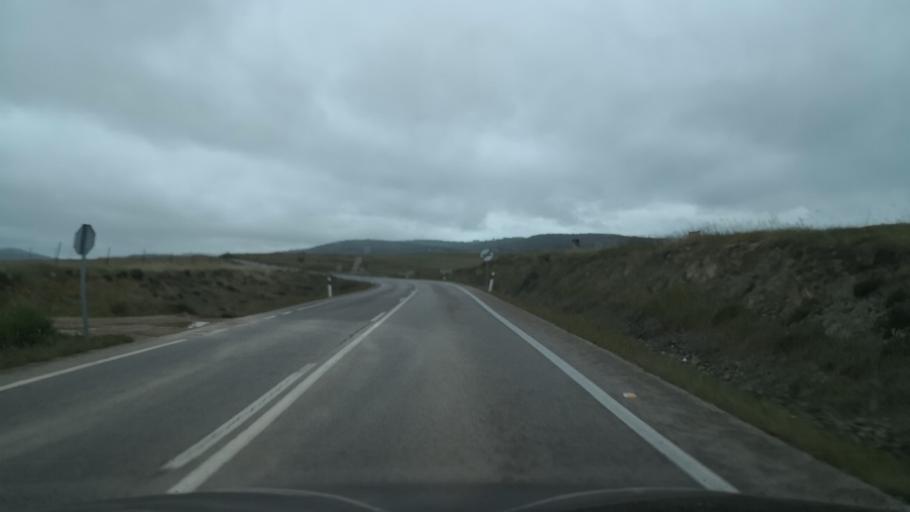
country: ES
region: Extremadura
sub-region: Provincia de Caceres
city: Casar de Caceres
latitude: 39.5193
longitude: -6.3980
